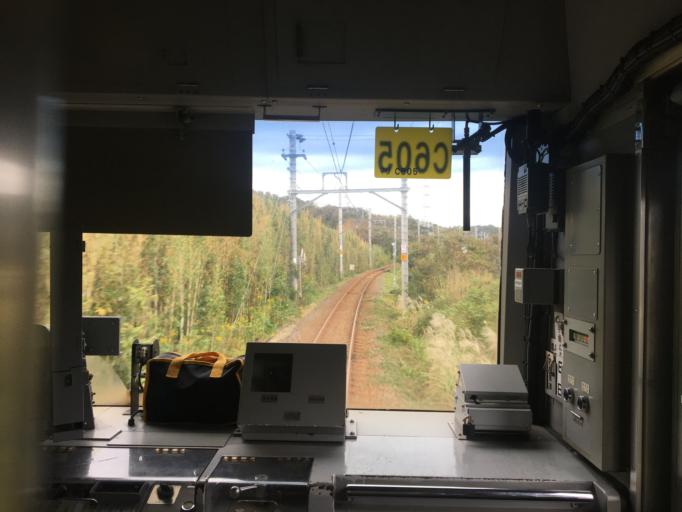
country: JP
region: Chiba
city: Tateyama
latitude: 34.9826
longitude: 139.9427
